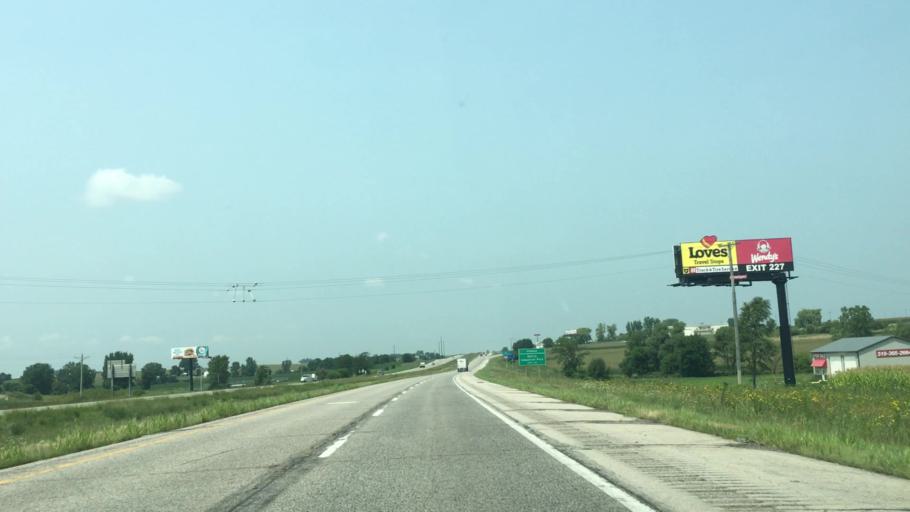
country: US
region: Iowa
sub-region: Benton County
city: Urbana
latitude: 42.2371
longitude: -91.8805
